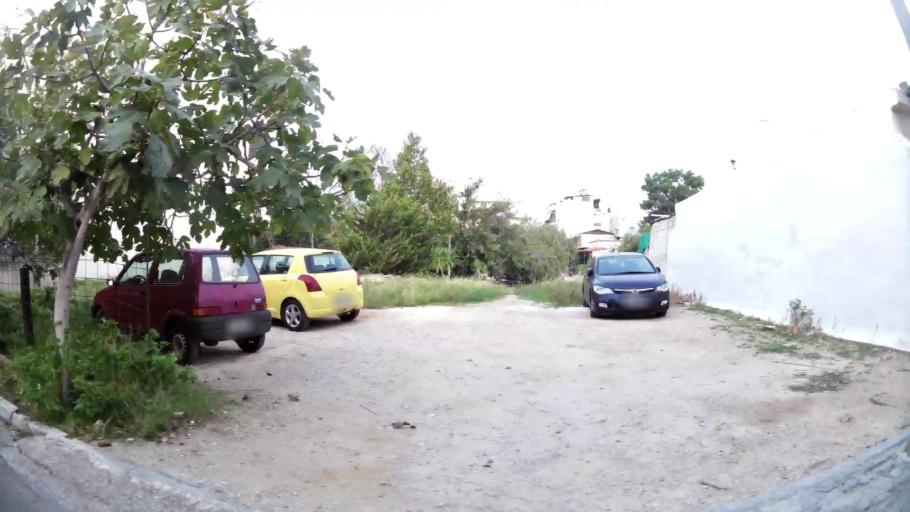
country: GR
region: Attica
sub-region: Nomarchia Athinas
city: Agios Dimitrios
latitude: 37.9299
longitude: 23.7284
